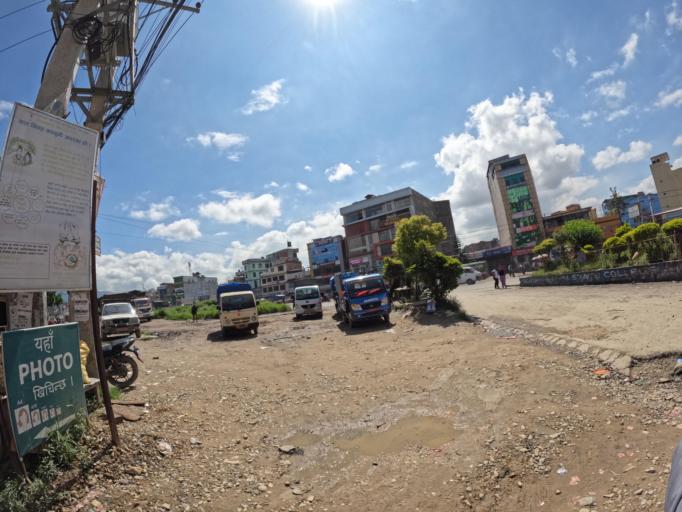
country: NP
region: Central Region
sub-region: Bagmati Zone
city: Kathmandu
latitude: 27.7387
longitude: 85.3257
